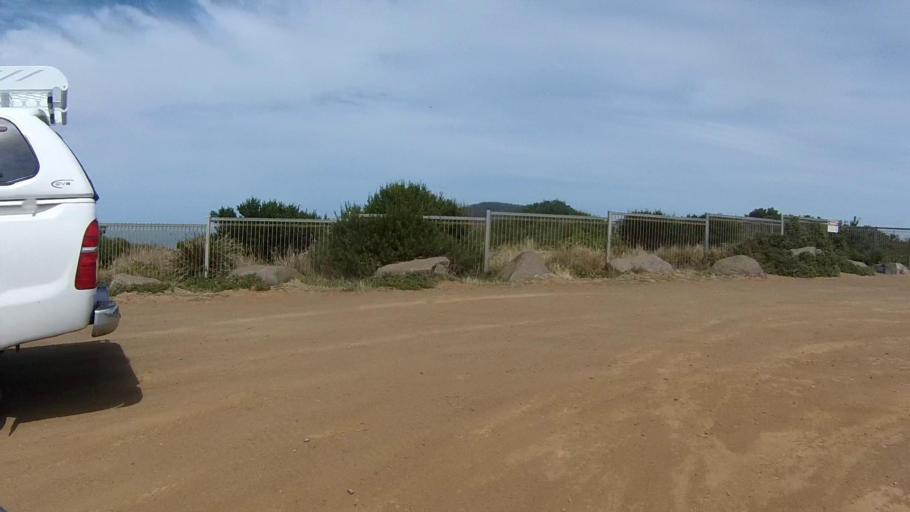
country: AU
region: Tasmania
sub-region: Clarence
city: Sandford
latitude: -43.0282
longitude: 147.4823
